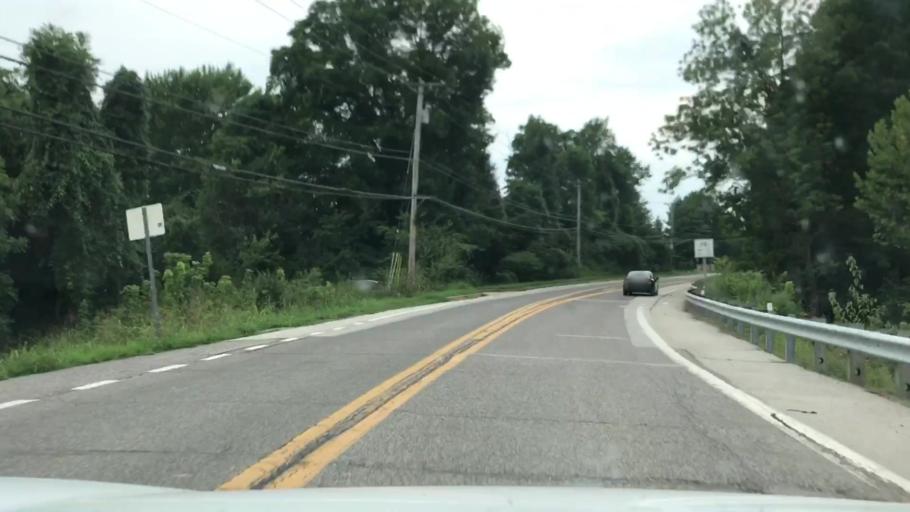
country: US
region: Missouri
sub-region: Saint Louis County
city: Chesterfield
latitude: 38.6542
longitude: -90.5965
